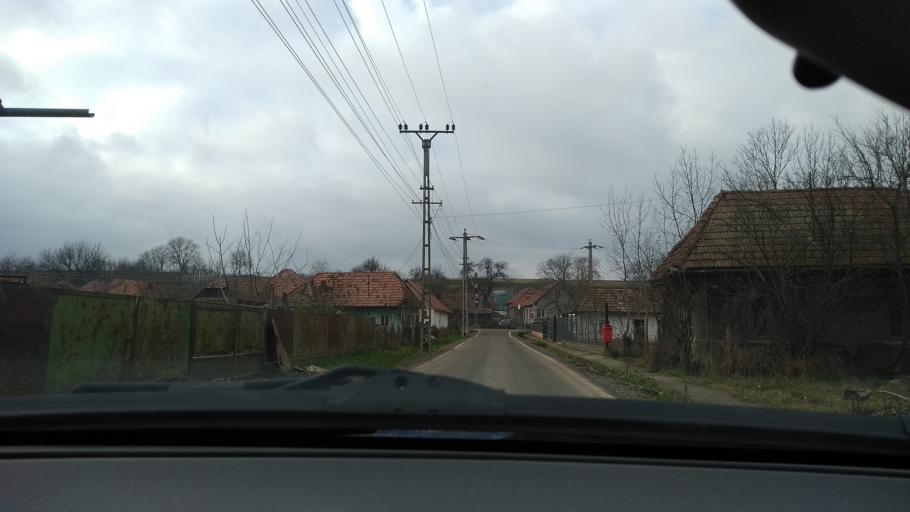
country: RO
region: Mures
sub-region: Comuna Panet
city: Panet
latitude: 46.5476
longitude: 24.4701
